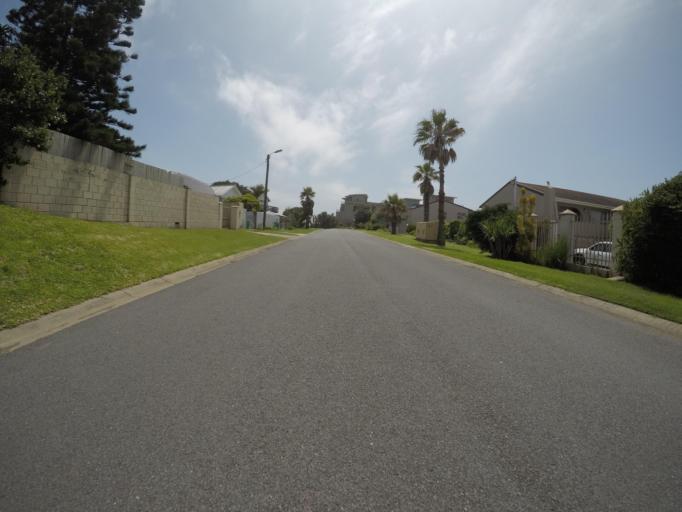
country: ZA
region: Eastern Cape
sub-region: Buffalo City Metropolitan Municipality
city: East London
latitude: -32.9408
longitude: 28.0313
